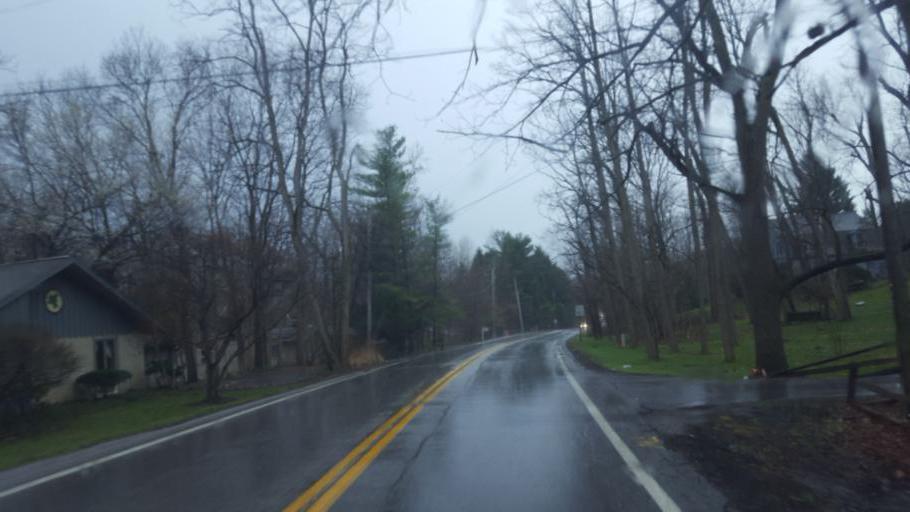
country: US
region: Ohio
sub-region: Franklin County
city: Worthington
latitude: 40.1316
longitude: -83.0359
